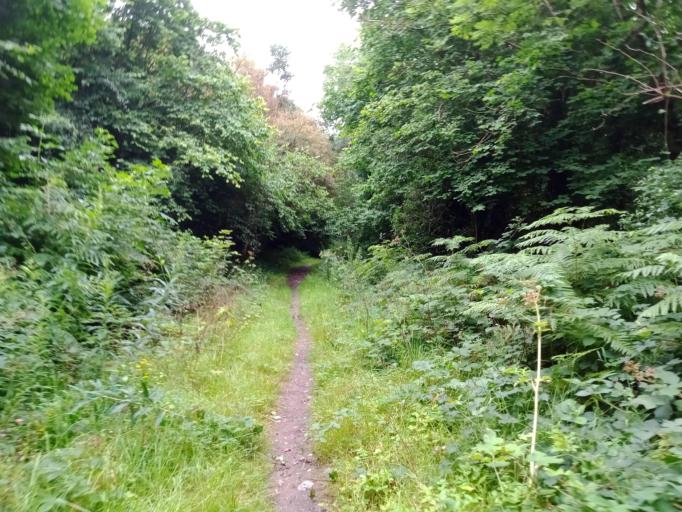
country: IE
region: Leinster
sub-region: Kilkenny
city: Ballyragget
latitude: 52.8257
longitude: -7.4016
